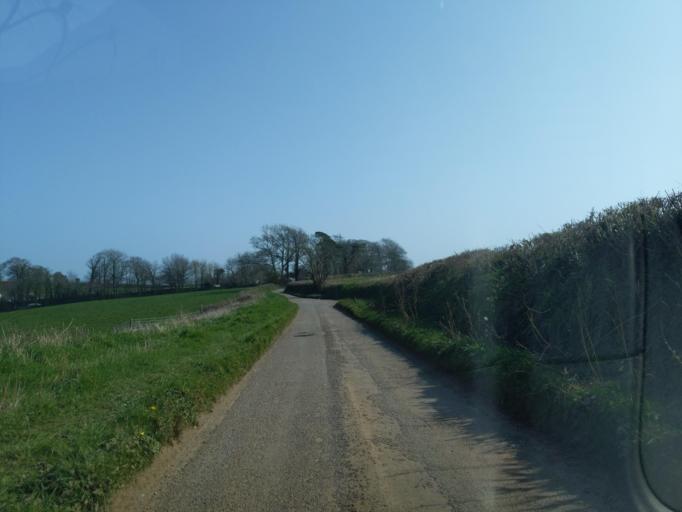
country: GB
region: England
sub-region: Devon
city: Totnes
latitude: 50.4256
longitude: -3.7041
